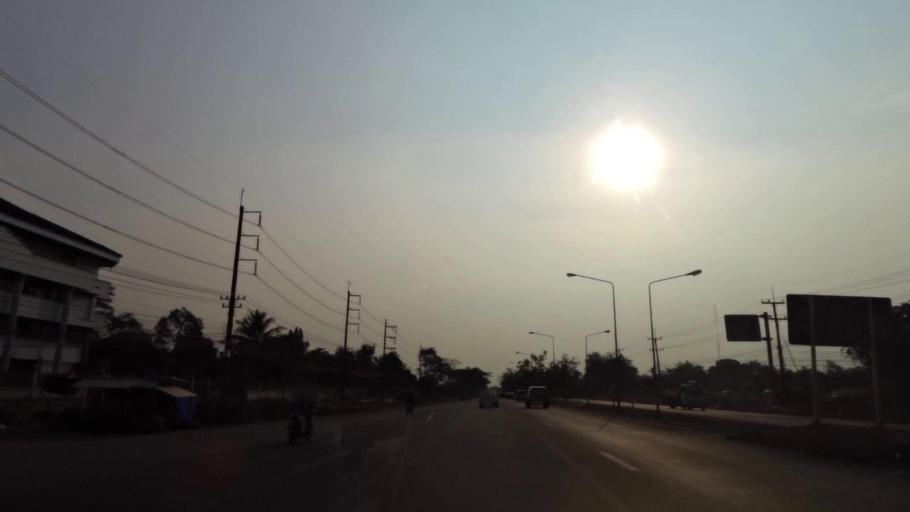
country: TH
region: Chanthaburi
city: Chanthaburi
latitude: 12.6134
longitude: 102.1384
